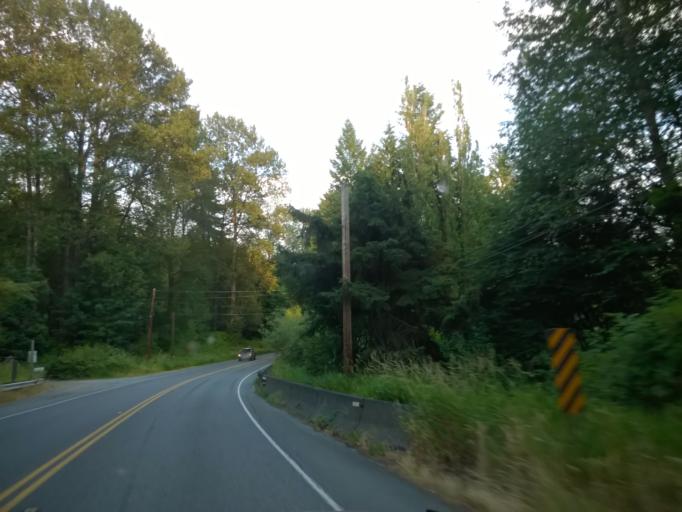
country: US
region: Washington
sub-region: King County
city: Cottage Lake
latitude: 47.7548
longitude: -122.0551
